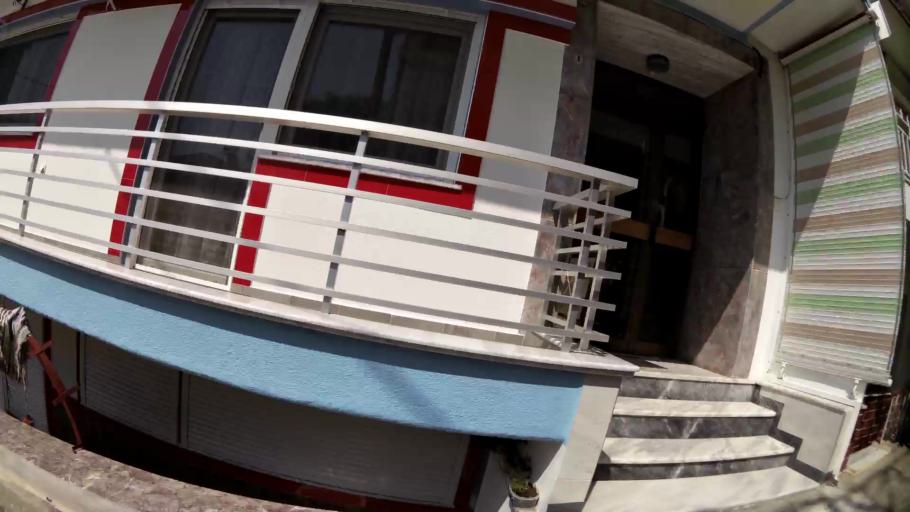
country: GR
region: Central Macedonia
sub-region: Nomos Thessalonikis
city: Polichni
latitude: 40.6646
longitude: 22.9440
